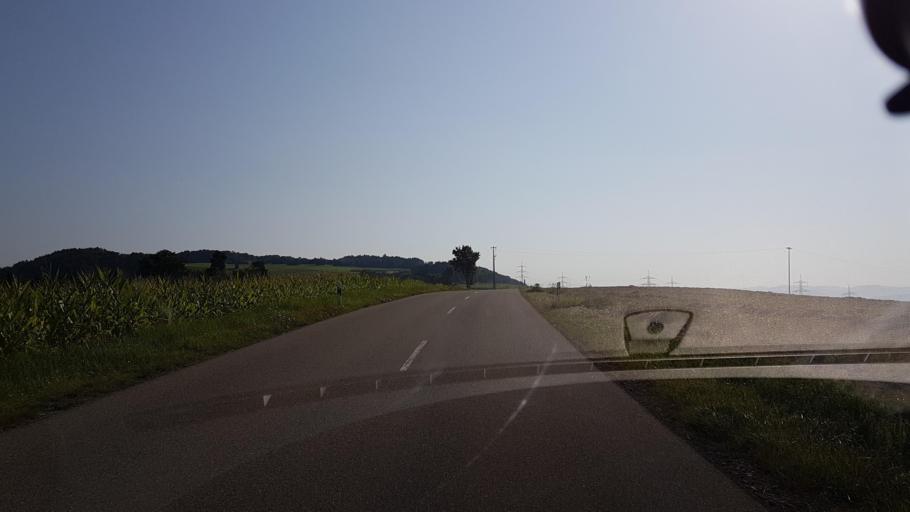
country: DE
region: Baden-Wuerttemberg
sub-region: Freiburg Region
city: Gorwihl
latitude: 47.6230
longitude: 8.1054
